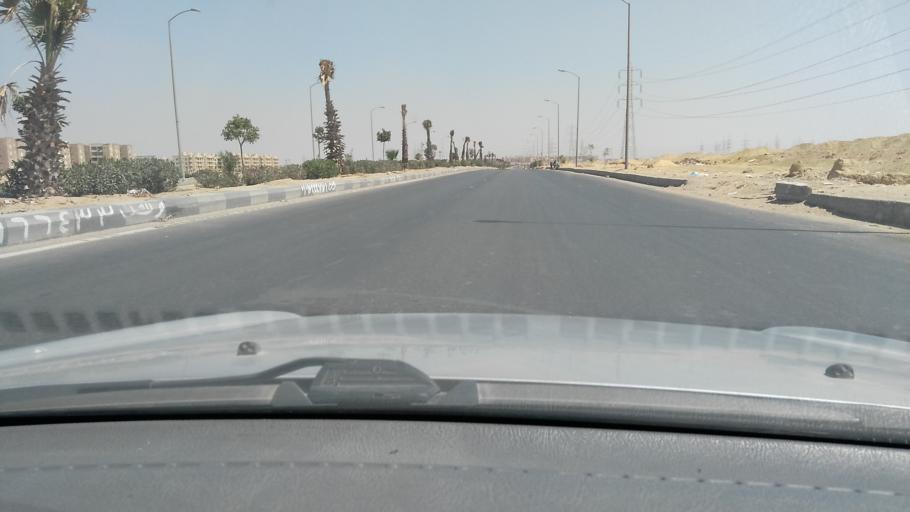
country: EG
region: Al Jizah
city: Madinat Sittah Uktubar
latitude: 29.9352
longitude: 30.9452
